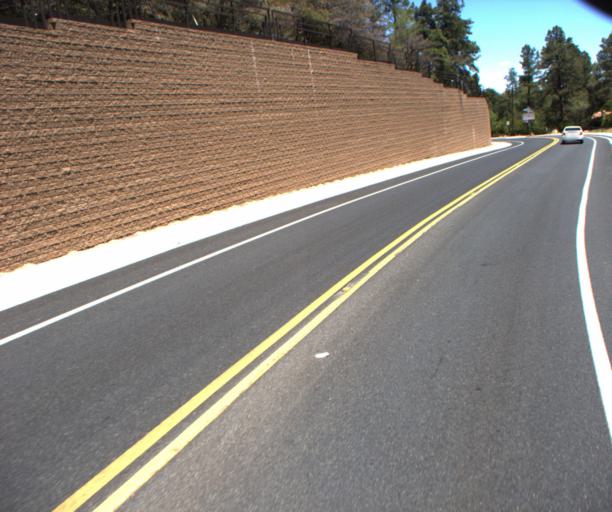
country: US
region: Arizona
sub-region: Yavapai County
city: Prescott
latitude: 34.5241
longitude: -112.4801
